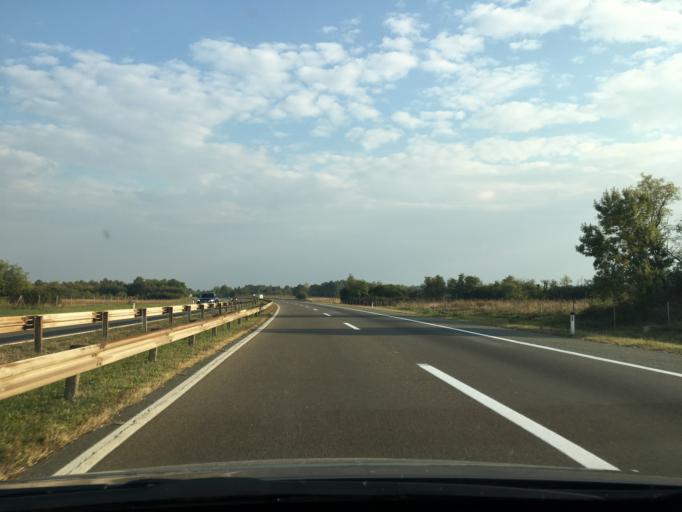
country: RS
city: Lugavcina
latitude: 44.5436
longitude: 20.9891
